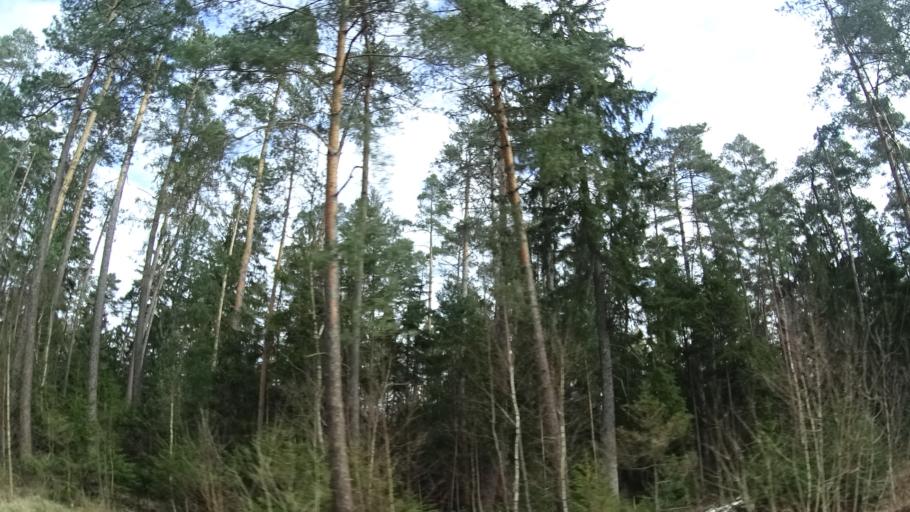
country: DE
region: Bavaria
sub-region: Regierungsbezirk Mittelfranken
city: Winkelhaid
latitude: 49.4097
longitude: 11.2868
